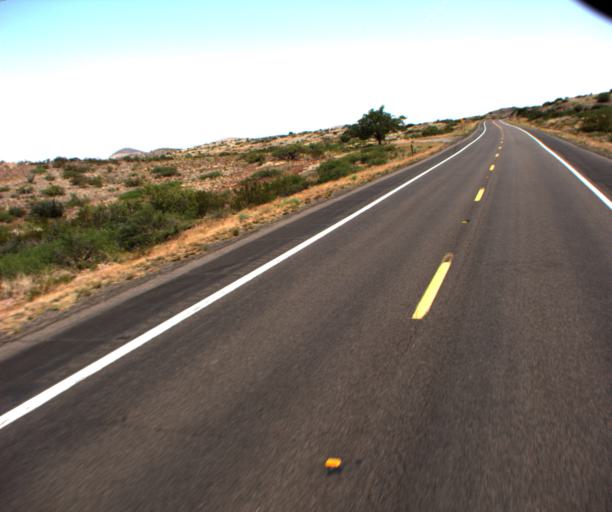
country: US
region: Arizona
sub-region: Greenlee County
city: Clifton
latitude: 32.7636
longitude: -109.2502
